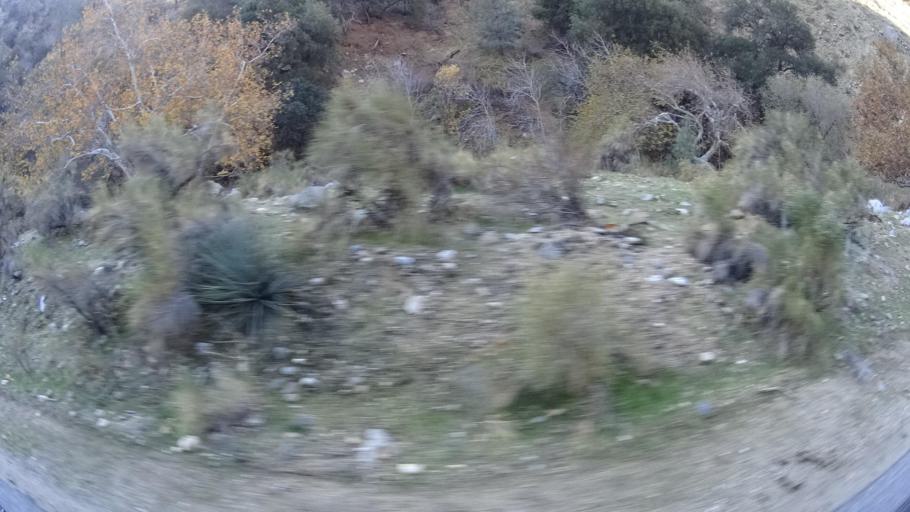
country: US
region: California
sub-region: Kern County
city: Golden Hills
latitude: 35.3146
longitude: -118.5357
